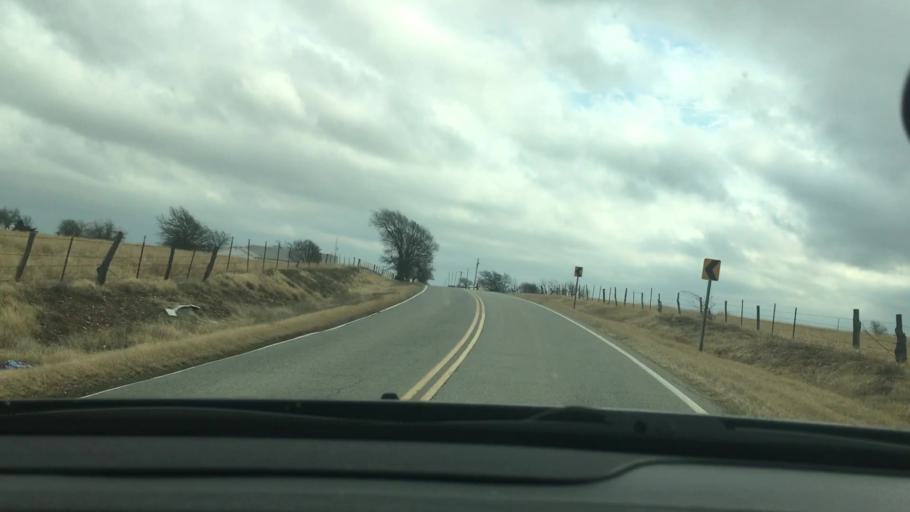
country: US
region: Oklahoma
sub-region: Bryan County
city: Durant
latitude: 34.0888
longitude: -96.4826
